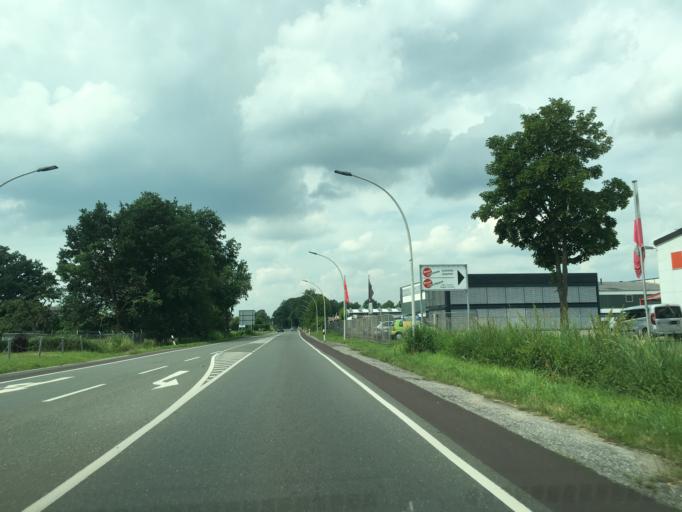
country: DE
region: North Rhine-Westphalia
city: Emsdetten
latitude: 52.1747
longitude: 7.4988
